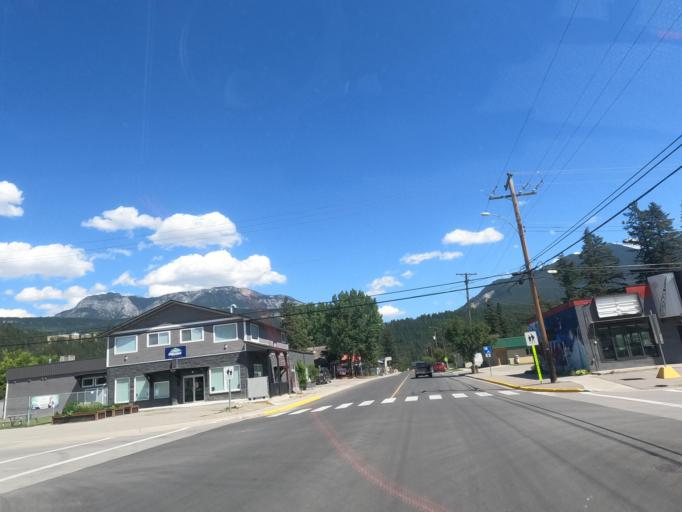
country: CA
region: British Columbia
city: Golden
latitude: 51.2962
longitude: -116.9617
